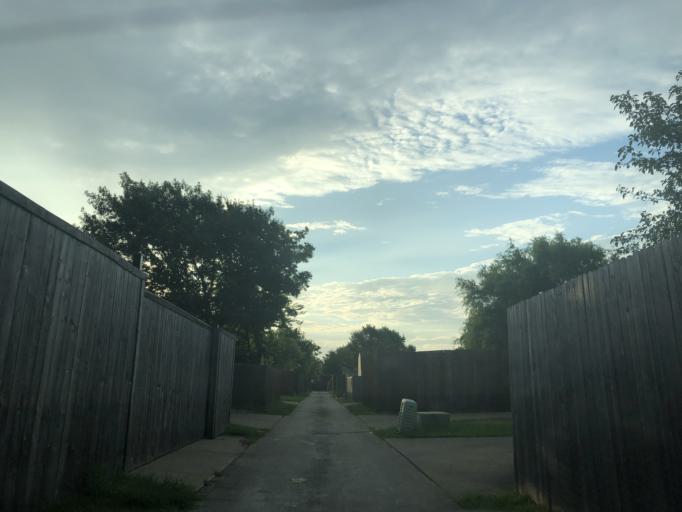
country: US
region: Texas
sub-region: Dallas County
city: Sunnyvale
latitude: 32.8476
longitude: -96.5586
